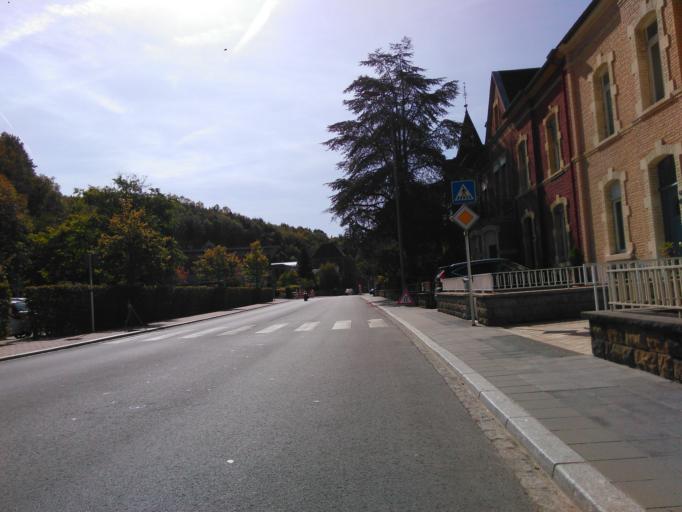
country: LU
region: Luxembourg
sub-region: Canton d'Esch-sur-Alzette
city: Rumelange
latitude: 49.4580
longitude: 6.0310
